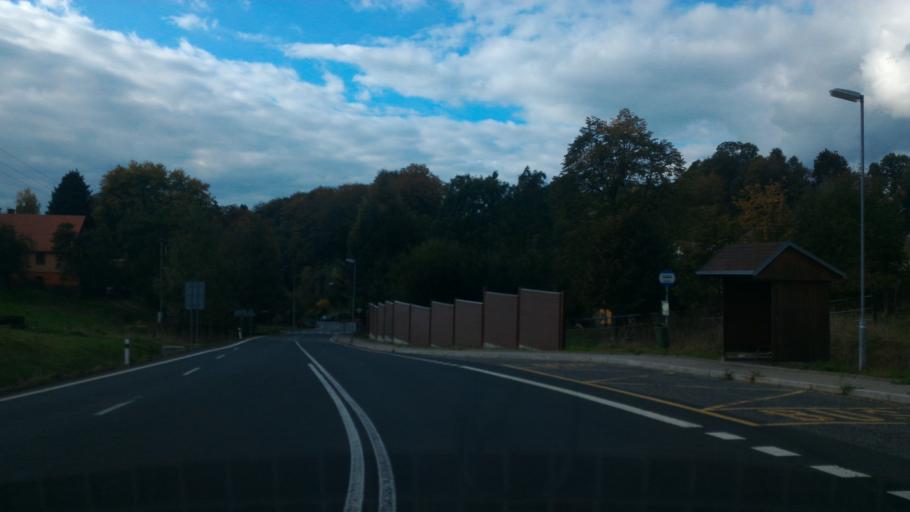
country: CZ
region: Ustecky
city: Ceska Kamenice
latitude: 50.8178
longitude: 14.4516
